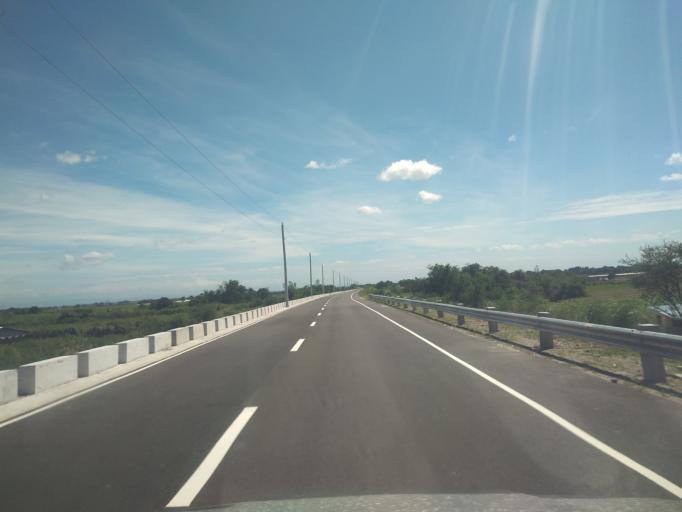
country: PH
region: Central Luzon
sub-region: Province of Pampanga
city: Pulung Santol
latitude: 15.0571
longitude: 120.5699
